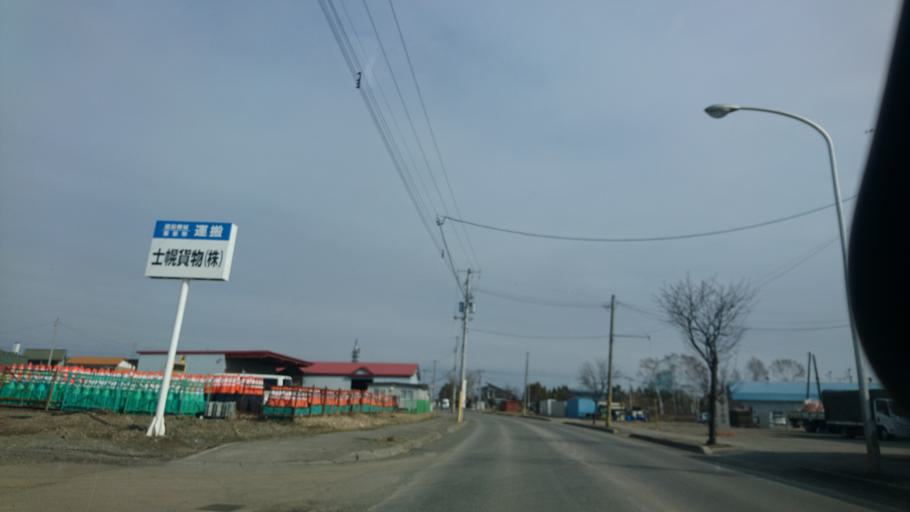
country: JP
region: Hokkaido
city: Obihiro
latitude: 42.9510
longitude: 143.2078
